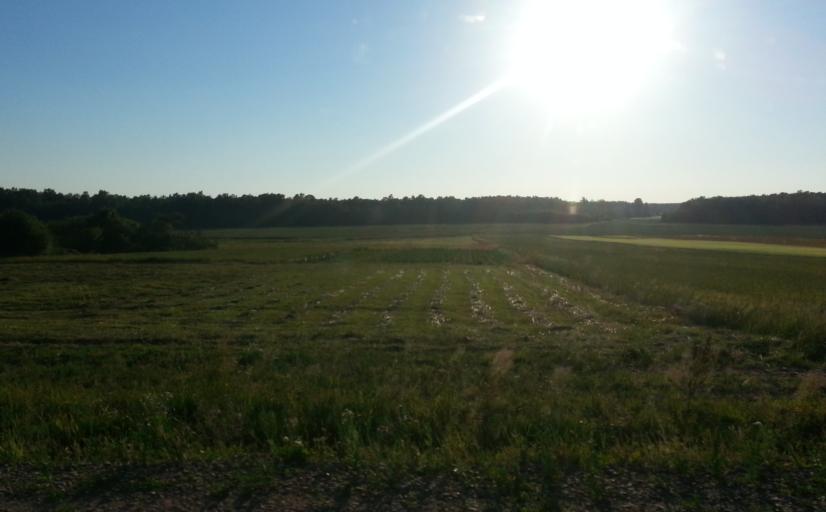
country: LT
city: Ramygala
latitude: 55.6030
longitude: 24.3475
